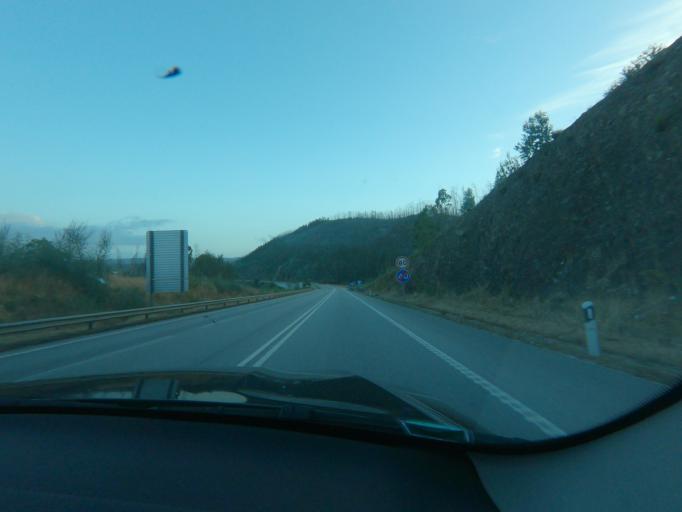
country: PT
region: Viseu
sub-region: Mortagua
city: Mortagua
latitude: 40.3359
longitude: -8.2258
